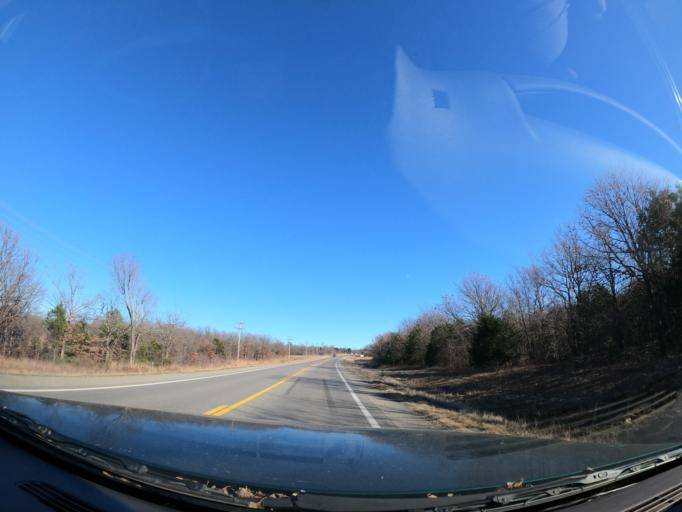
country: US
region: Oklahoma
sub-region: Pittsburg County
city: Longtown
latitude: 35.2392
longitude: -95.4759
